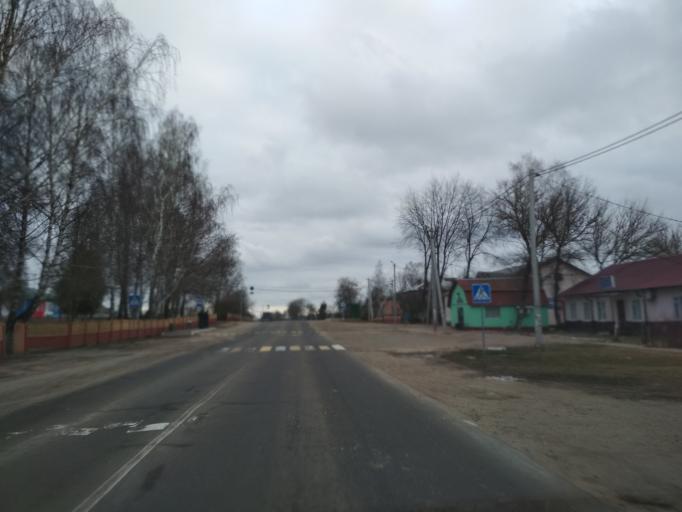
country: BY
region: Minsk
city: Svislach
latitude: 53.5709
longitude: 27.9608
